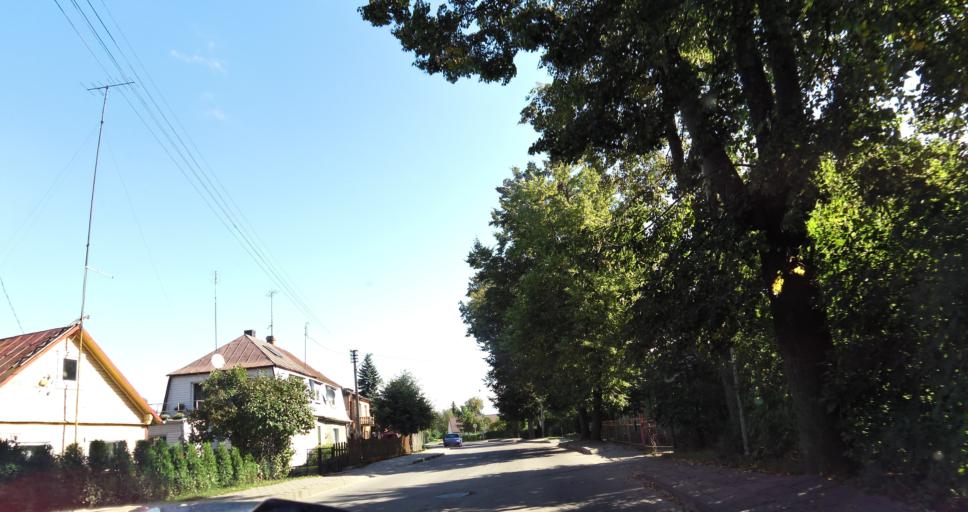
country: LT
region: Panevezys
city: Pasvalys
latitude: 56.0631
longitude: 24.4054
